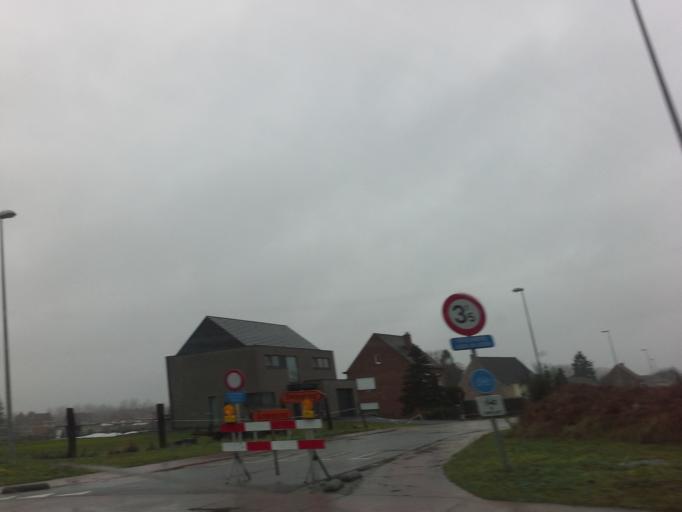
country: BE
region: Flanders
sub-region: Provincie Vlaams-Brabant
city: Scherpenheuvel-Zichem
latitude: 50.9934
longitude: 4.9436
